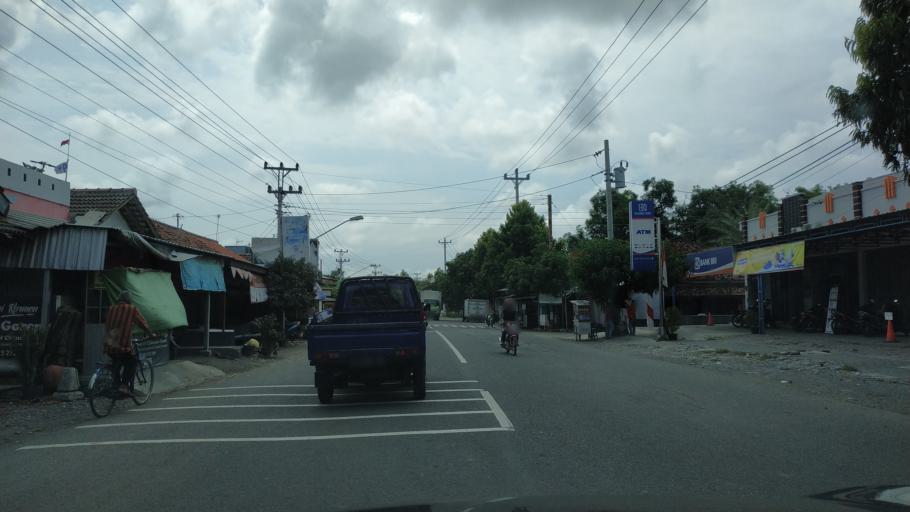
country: ID
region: Central Java
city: Tegal
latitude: -6.9005
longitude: 109.1256
